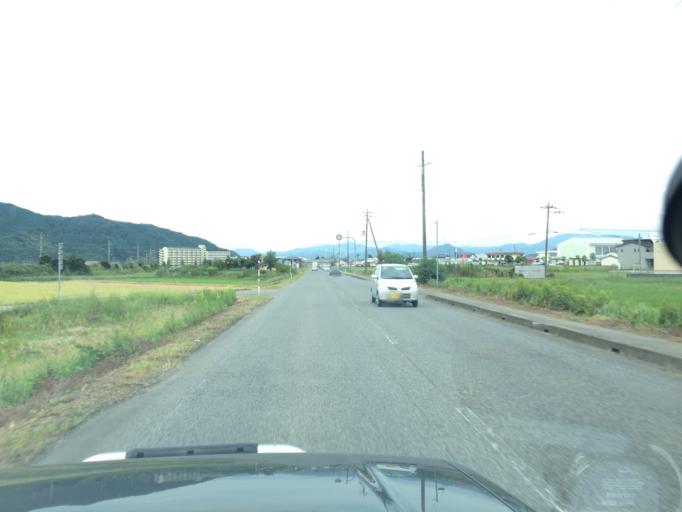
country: JP
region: Hyogo
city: Toyooka
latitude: 35.4896
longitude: 134.7962
